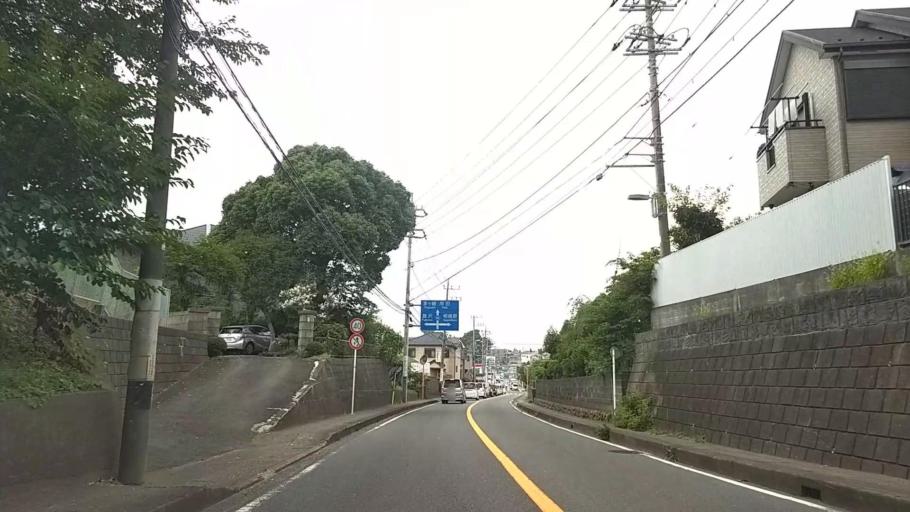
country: JP
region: Kanagawa
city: Minami-rinkan
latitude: 35.4313
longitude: 139.4378
